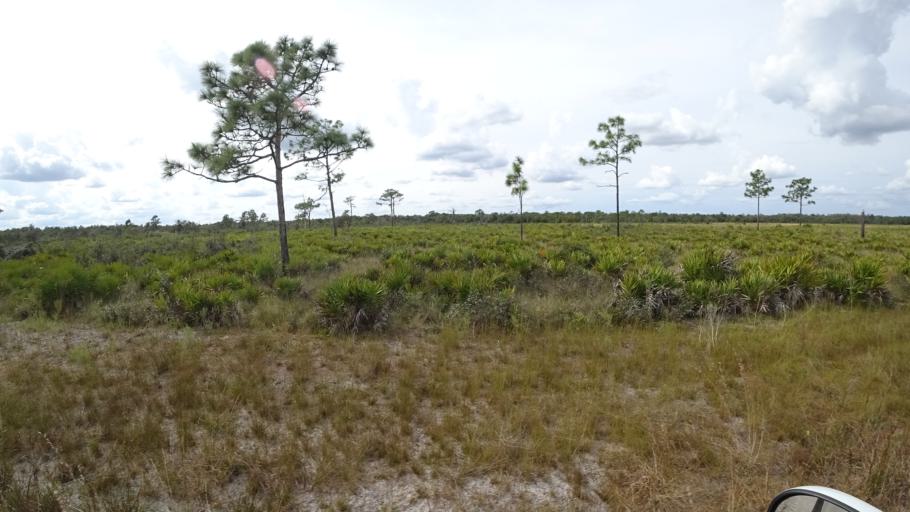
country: US
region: Florida
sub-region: Hillsborough County
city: Wimauma
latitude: 27.5563
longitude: -82.1432
